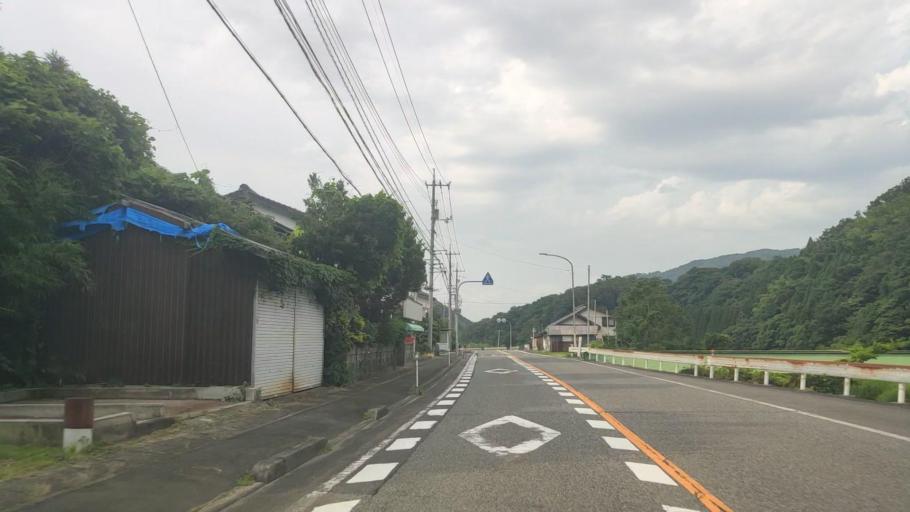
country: JP
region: Tottori
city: Kurayoshi
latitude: 35.3557
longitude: 133.8456
